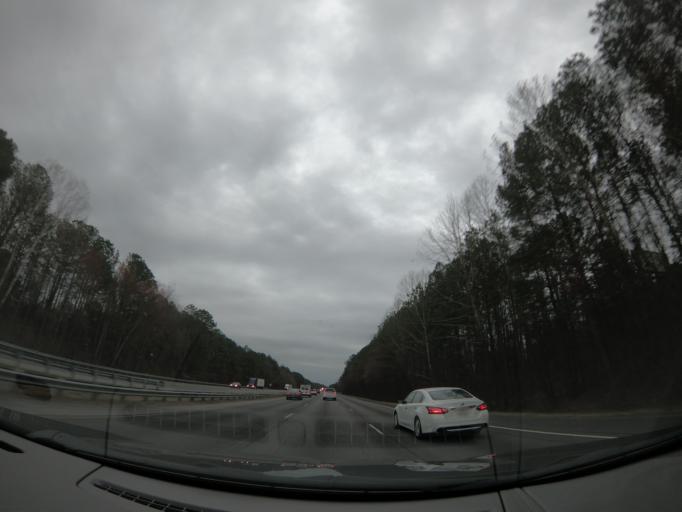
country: US
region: Georgia
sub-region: Gordon County
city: Calhoun
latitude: 34.6320
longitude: -84.9751
